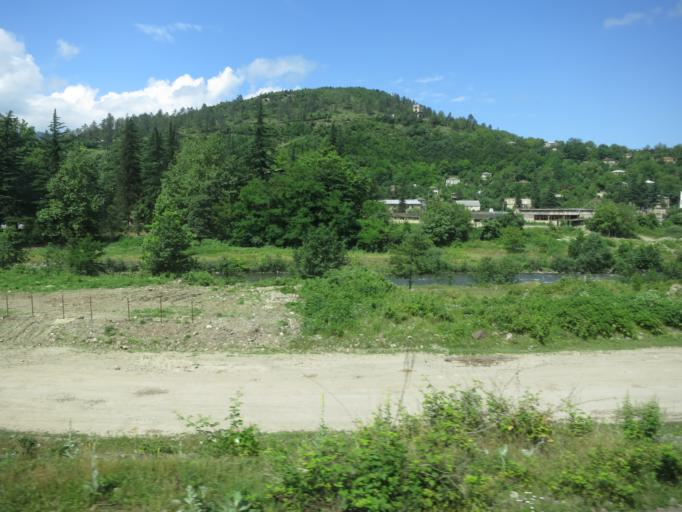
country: GE
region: Imereti
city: Kharagauli
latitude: 42.0153
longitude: 43.2066
